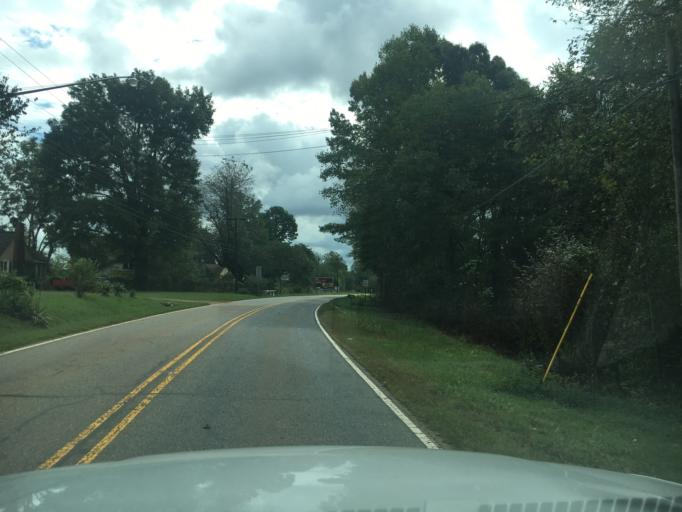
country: US
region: North Carolina
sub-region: Catawba County
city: Saint Stephens
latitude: 35.7316
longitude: -81.2870
